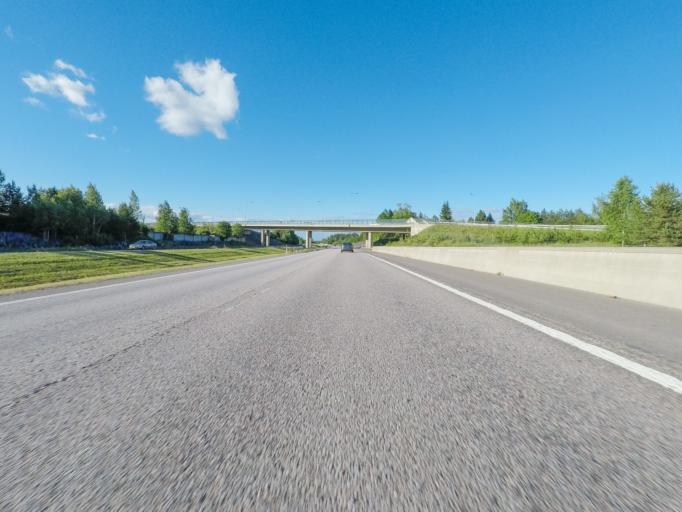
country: FI
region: Uusimaa
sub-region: Helsinki
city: Maentsaelae
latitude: 60.6439
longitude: 25.3053
